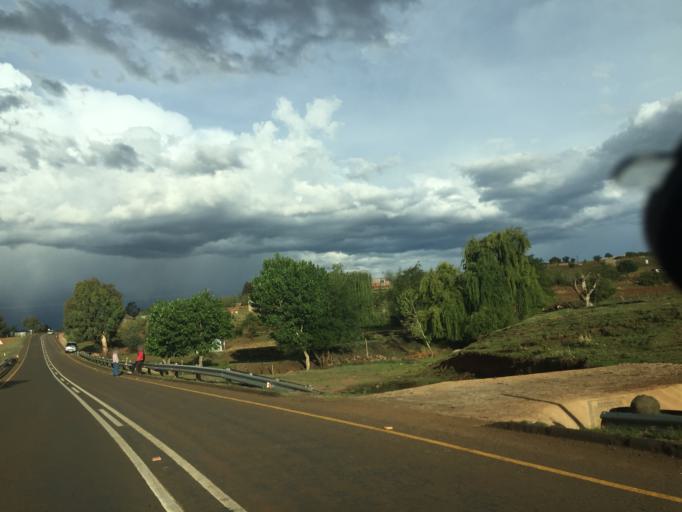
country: LS
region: Berea
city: Teyateyaneng
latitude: -29.1648
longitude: 28.0238
